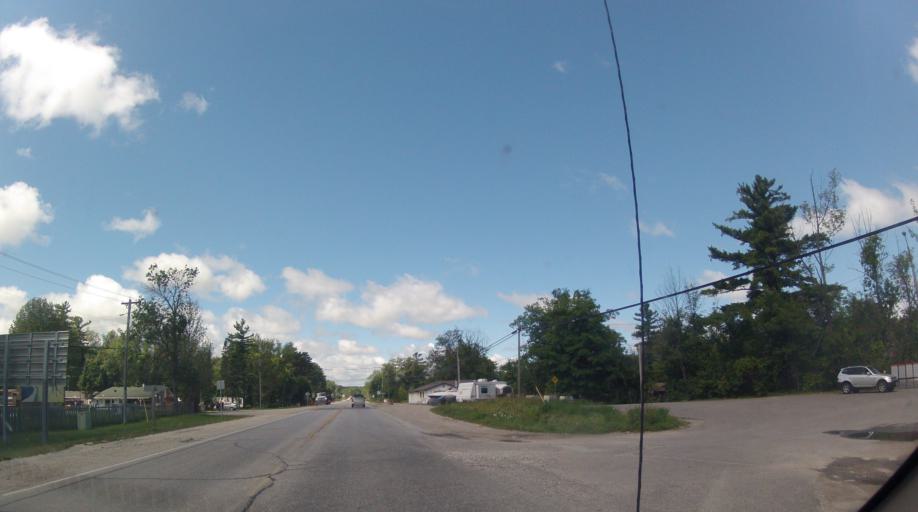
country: CA
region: Ontario
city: Collingwood
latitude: 44.4682
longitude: -80.1123
